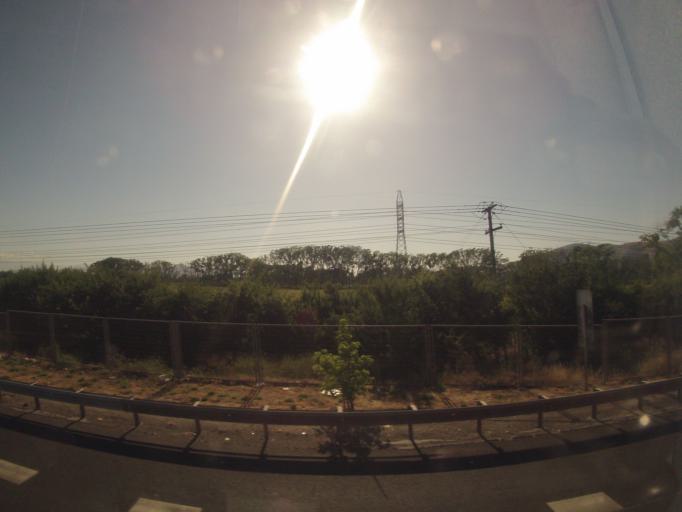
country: CL
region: Santiago Metropolitan
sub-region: Provincia de Maipo
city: San Bernardo
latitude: -33.6204
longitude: -70.7151
